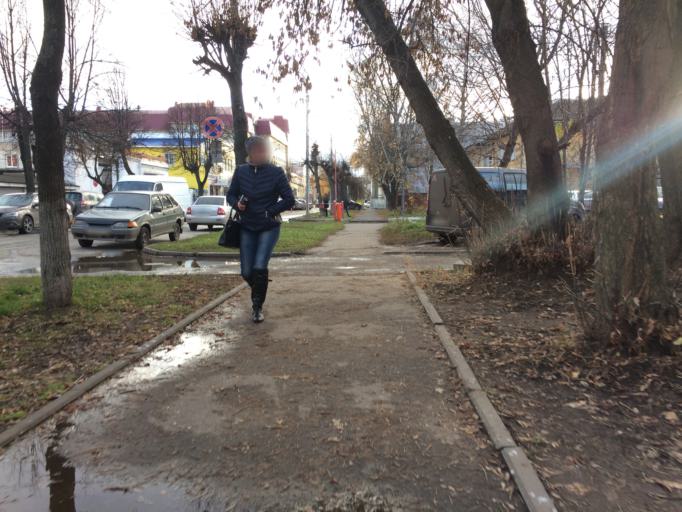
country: RU
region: Mariy-El
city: Yoshkar-Ola
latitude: 56.6392
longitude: 47.8977
